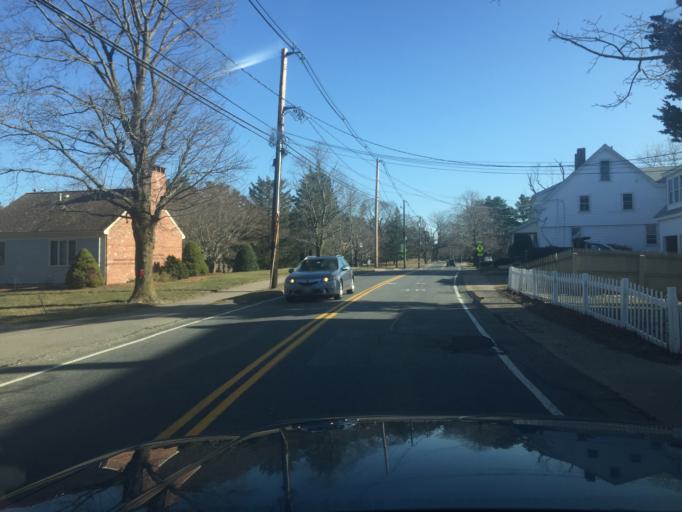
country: US
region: Massachusetts
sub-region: Norfolk County
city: Millis-Clicquot
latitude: 42.1651
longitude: -71.3555
